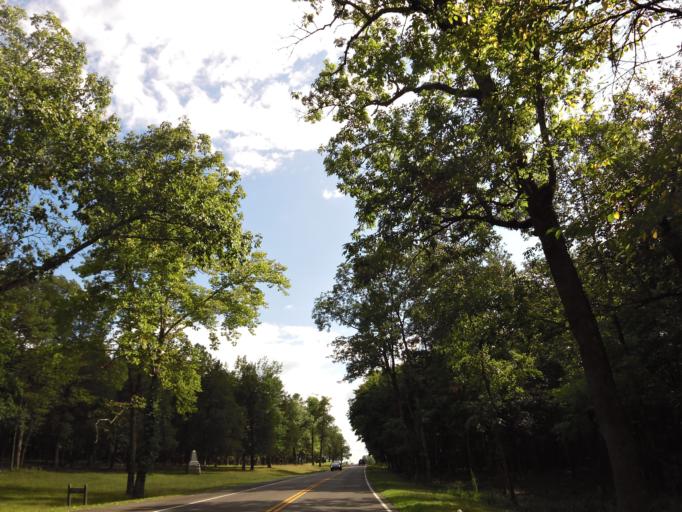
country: US
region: Georgia
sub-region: Walker County
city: Chickamauga
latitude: 34.8981
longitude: -85.2620
